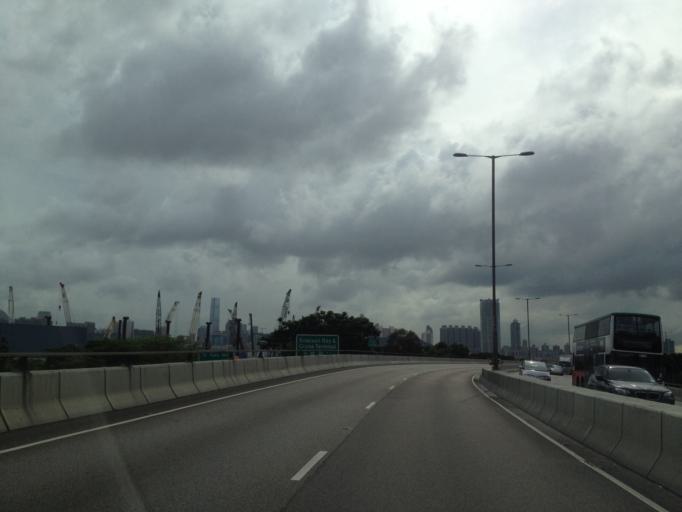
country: HK
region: Kowloon City
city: Kowloon
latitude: 22.3170
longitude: 114.2110
